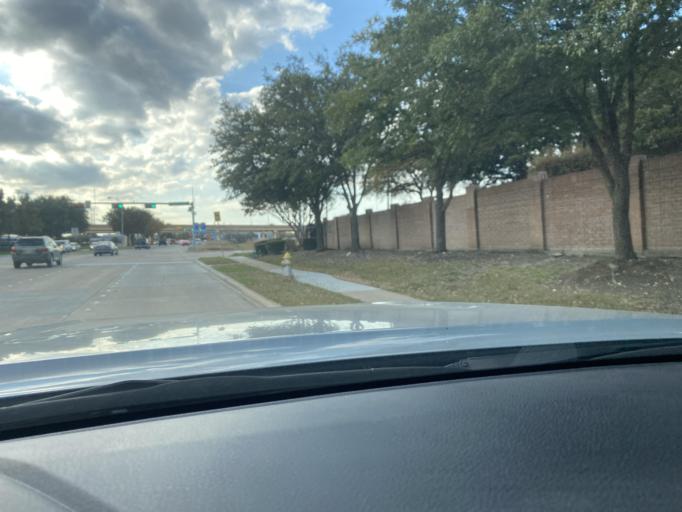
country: US
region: Texas
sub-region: Dallas County
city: Addison
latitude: 33.0166
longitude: -96.8260
